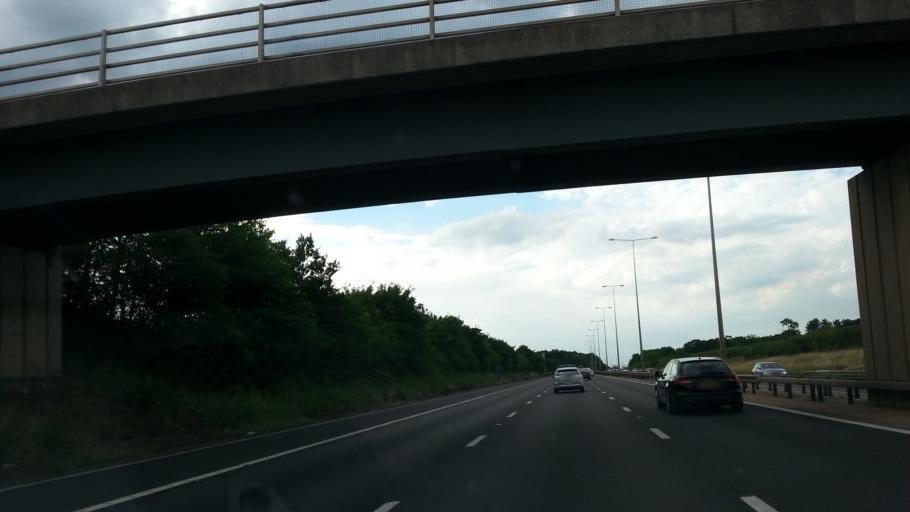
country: GB
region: England
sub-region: Worcestershire
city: Upton upon Severn
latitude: 52.0918
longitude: -2.1822
